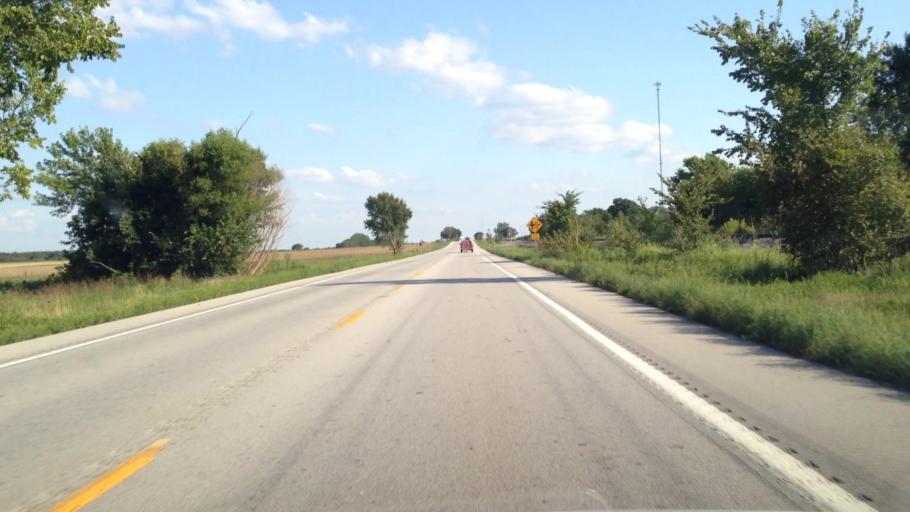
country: US
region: Missouri
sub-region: Jasper County
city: Carl Junction
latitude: 37.2663
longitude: -94.5968
